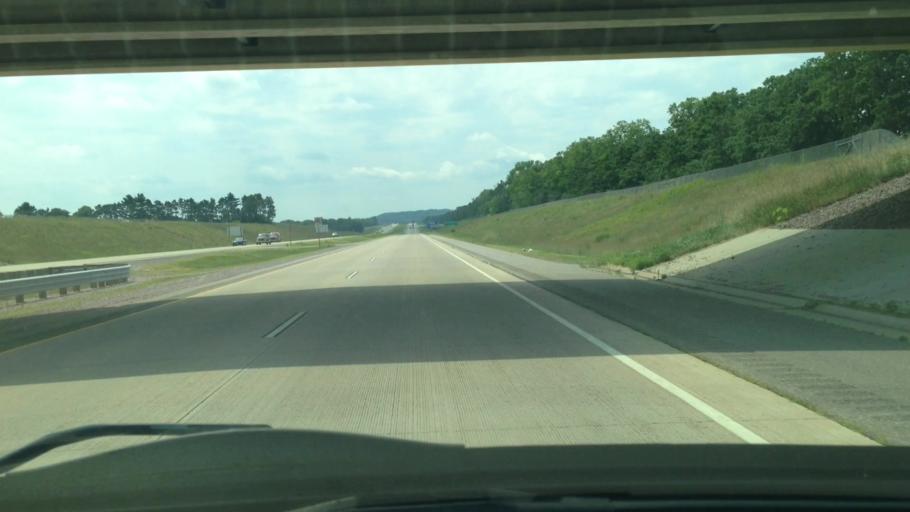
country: US
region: Wisconsin
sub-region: Sauk County
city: Lake Delton
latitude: 43.5472
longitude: -89.7873
